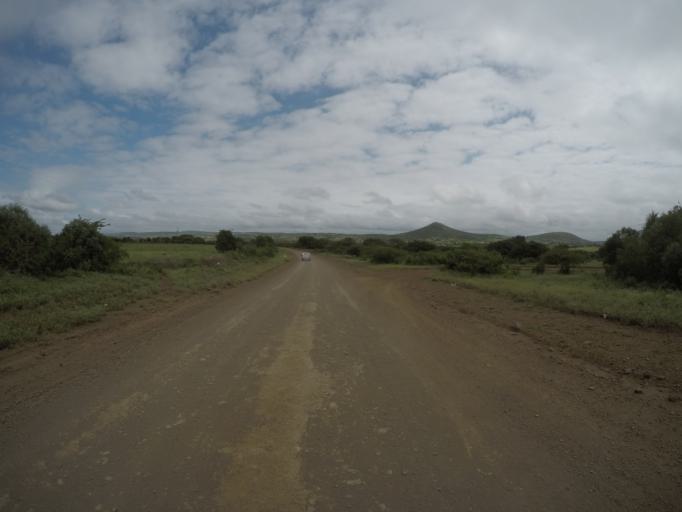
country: ZA
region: KwaZulu-Natal
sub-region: uThungulu District Municipality
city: Empangeni
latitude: -28.6222
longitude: 31.8669
